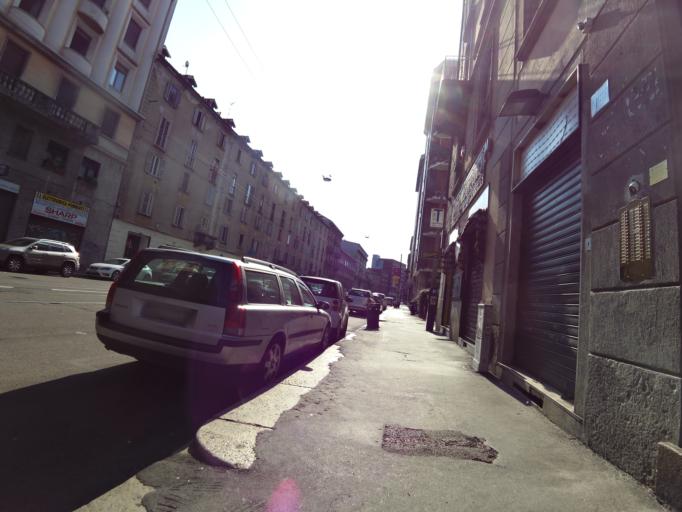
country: IT
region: Lombardy
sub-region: Citta metropolitana di Milano
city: Milano
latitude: 45.4511
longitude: 9.1932
